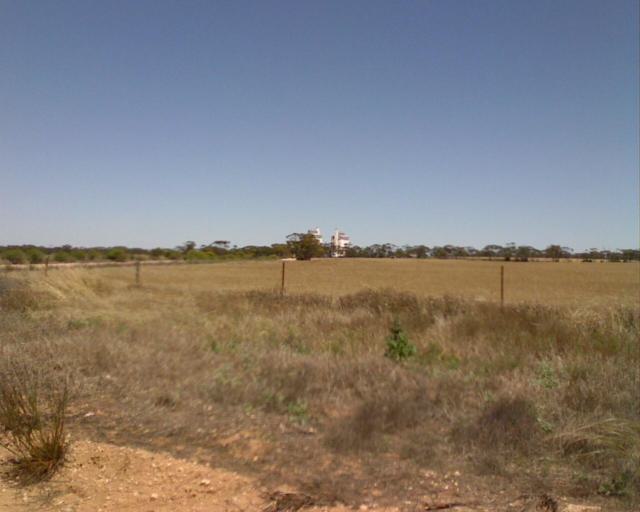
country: AU
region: South Australia
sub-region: Kimba
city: Caralue
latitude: -32.9480
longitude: 135.2831
